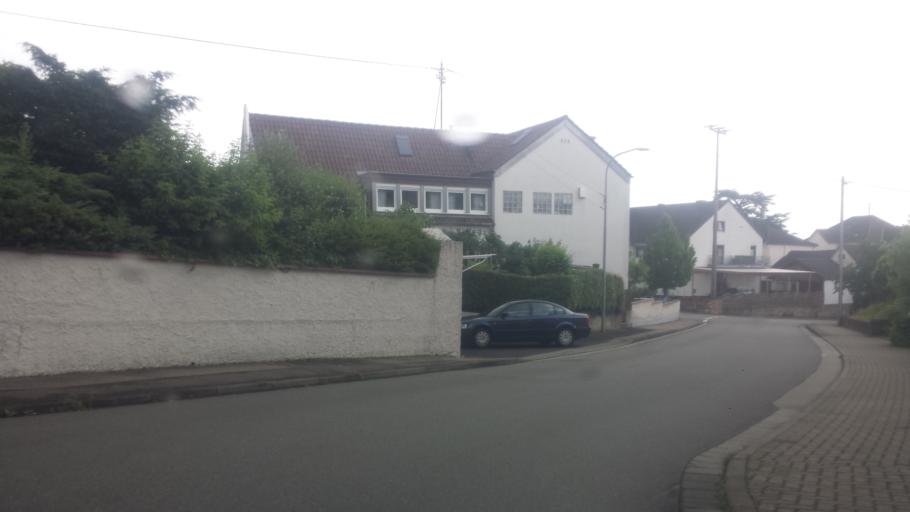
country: DE
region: Rheinland-Pfalz
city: Edenkoben
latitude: 49.2869
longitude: 8.1265
